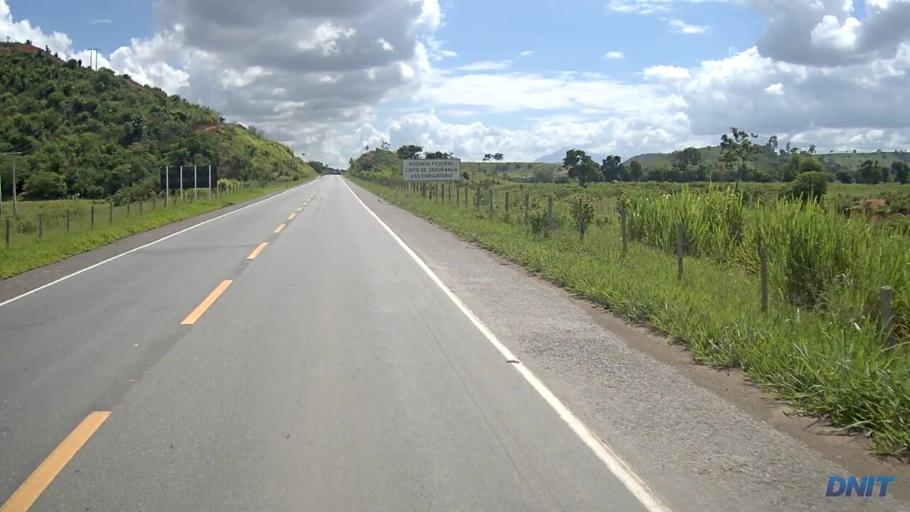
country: BR
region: Minas Gerais
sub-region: Governador Valadares
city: Governador Valadares
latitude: -18.9992
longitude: -42.1238
